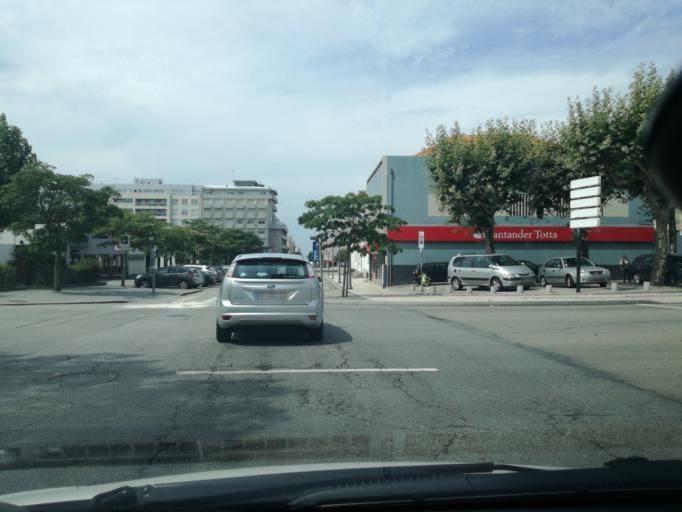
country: PT
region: Aveiro
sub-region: Espinho
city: Espinho
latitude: 41.0085
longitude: -8.6378
